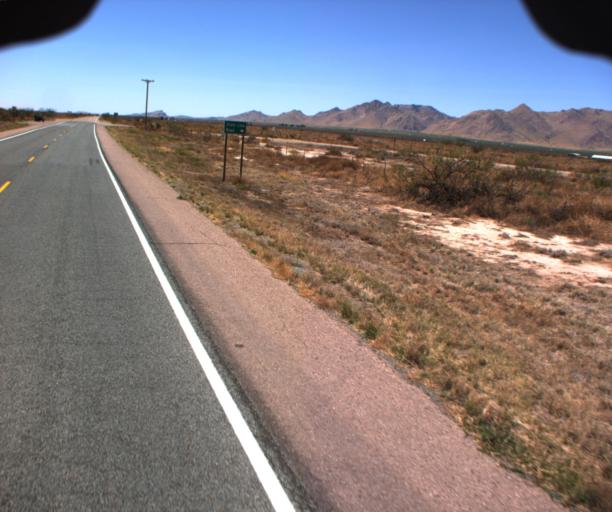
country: US
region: New Mexico
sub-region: Hidalgo County
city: Lordsburg
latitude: 31.8124
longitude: -109.0482
